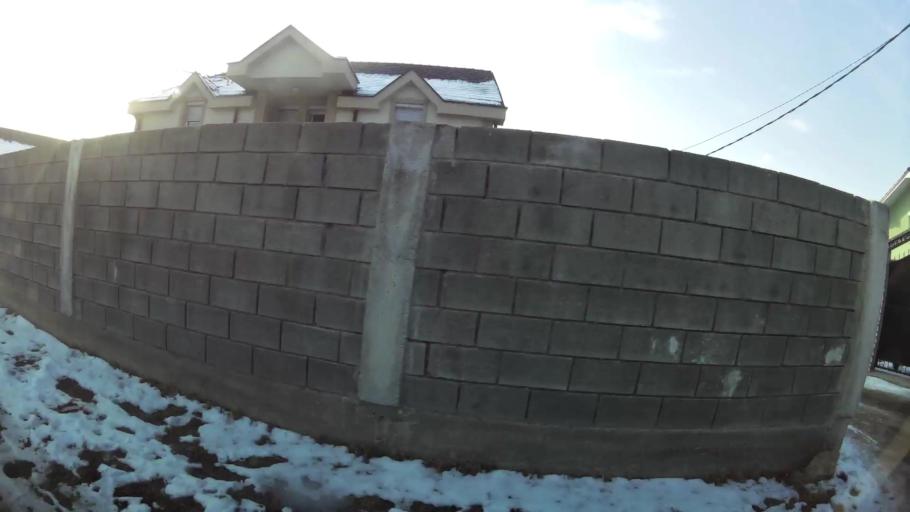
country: MK
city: Creshevo
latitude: 42.0239
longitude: 21.5105
